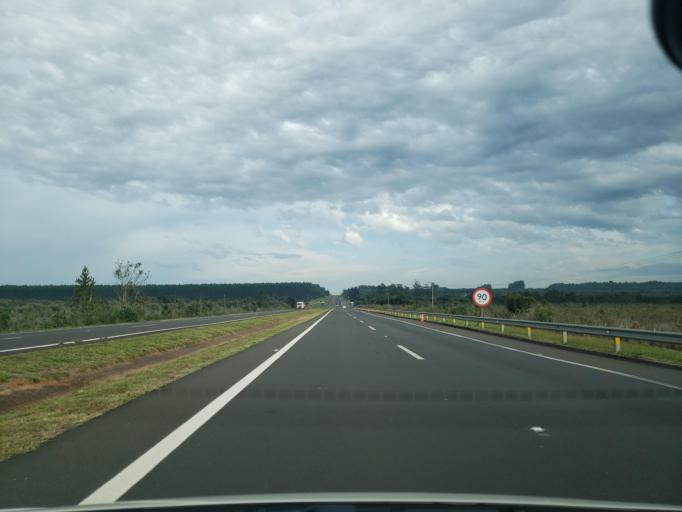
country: BR
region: Sao Paulo
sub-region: Itirapina
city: Itirapina
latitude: -22.2574
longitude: -47.8604
